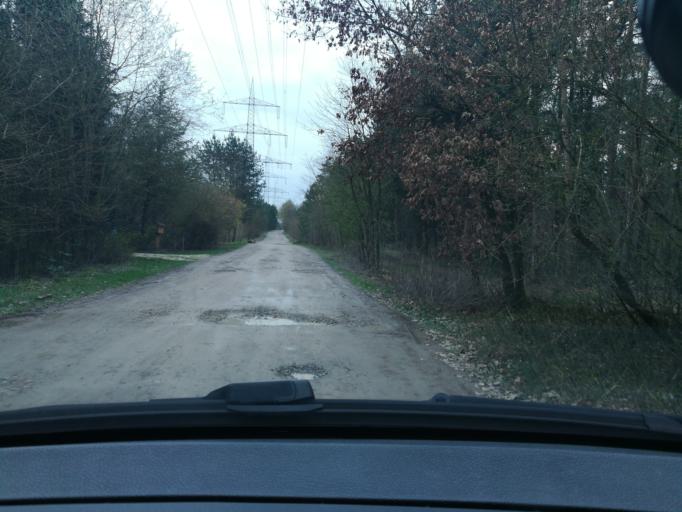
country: DE
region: North Rhine-Westphalia
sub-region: Regierungsbezirk Detmold
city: Oerlinghausen
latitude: 51.9489
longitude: 8.6186
